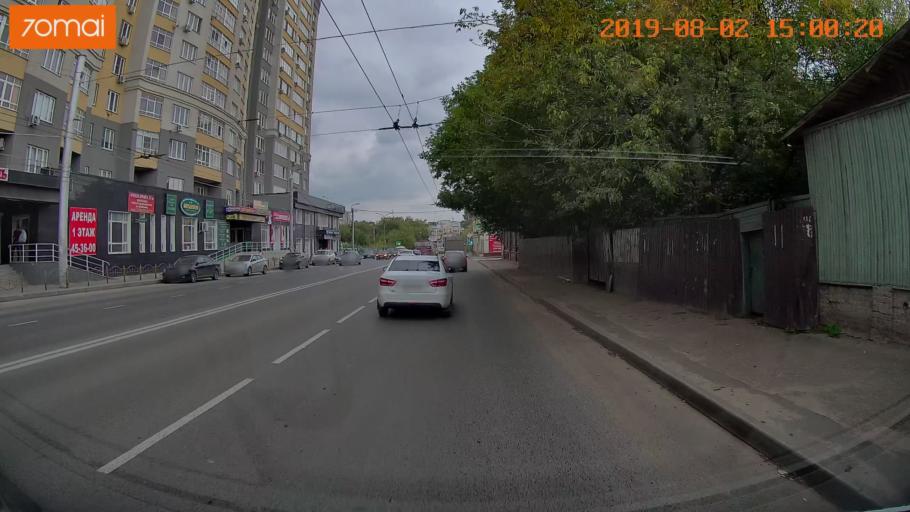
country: RU
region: Ivanovo
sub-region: Gorod Ivanovo
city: Ivanovo
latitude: 56.9996
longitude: 40.9674
